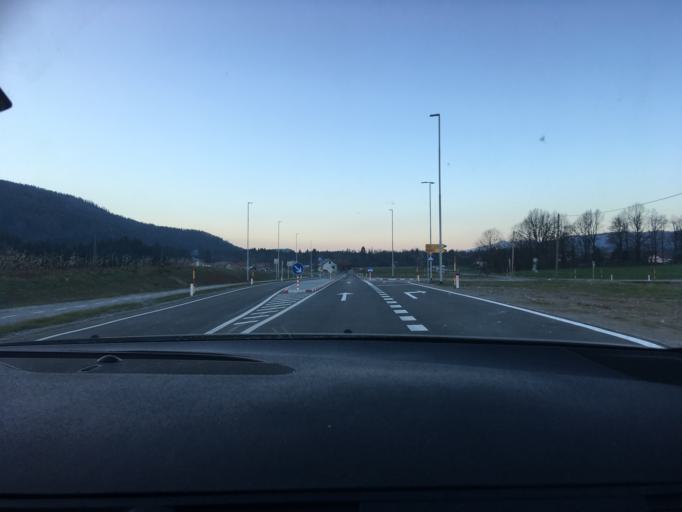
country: SI
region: Kocevje
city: Kocevje
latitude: 45.6715
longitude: 14.8349
